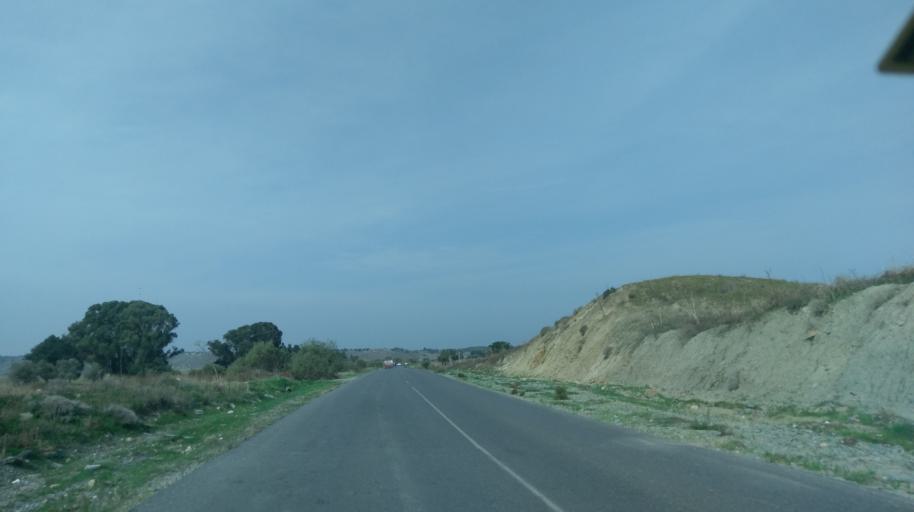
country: CY
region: Keryneia
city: Lapithos
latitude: 35.2825
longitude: 33.0956
